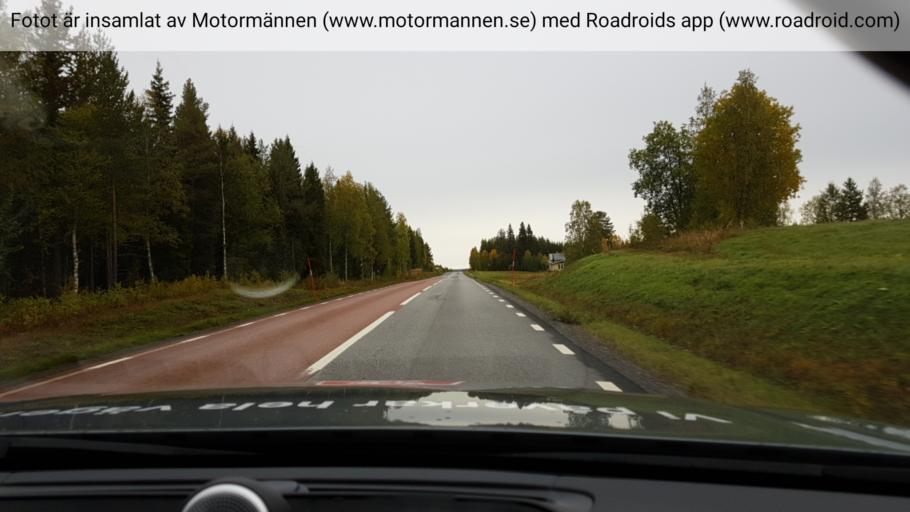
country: SE
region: Jaemtland
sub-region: Stroemsunds Kommun
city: Stroemsund
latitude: 63.7710
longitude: 15.5048
